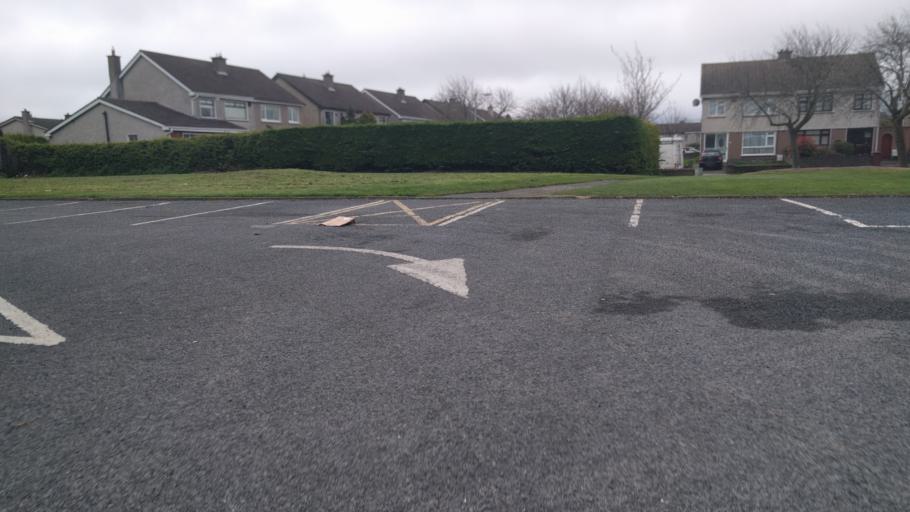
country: IE
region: Leinster
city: Tallaght
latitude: 53.2863
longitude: -6.3867
